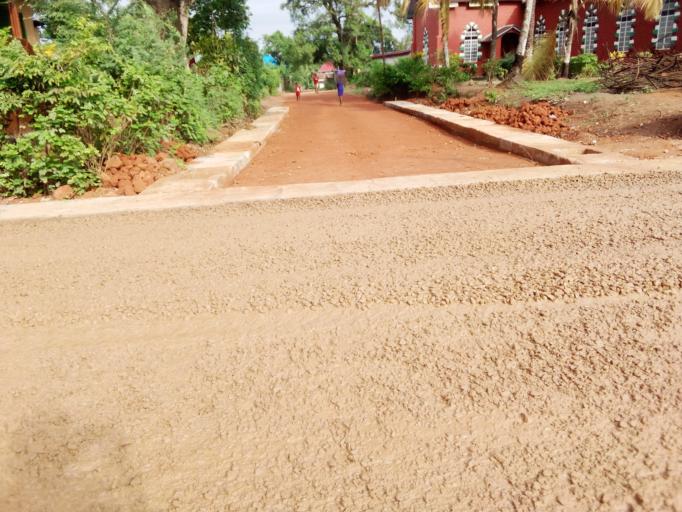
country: SL
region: Western Area
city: Waterloo
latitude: 8.3406
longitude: -13.0701
